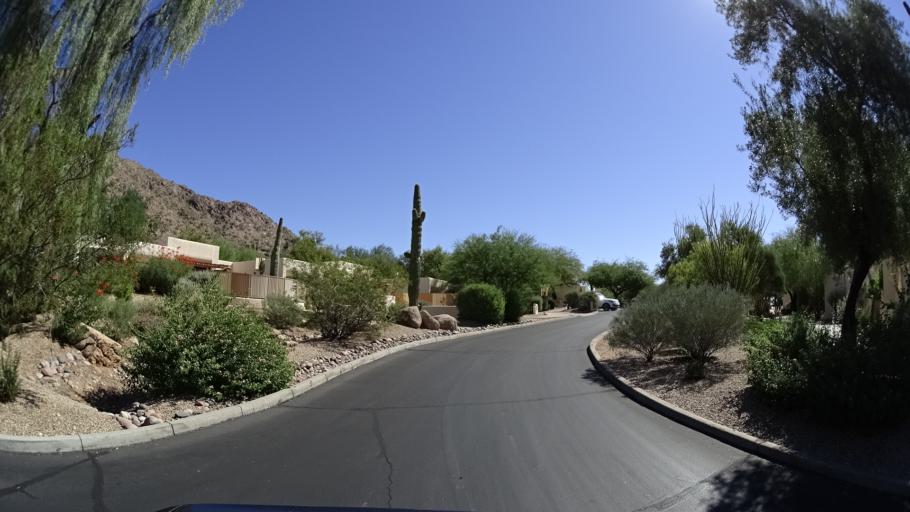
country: US
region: Arizona
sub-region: Maricopa County
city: Paradise Valley
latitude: 33.5368
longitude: -111.9654
